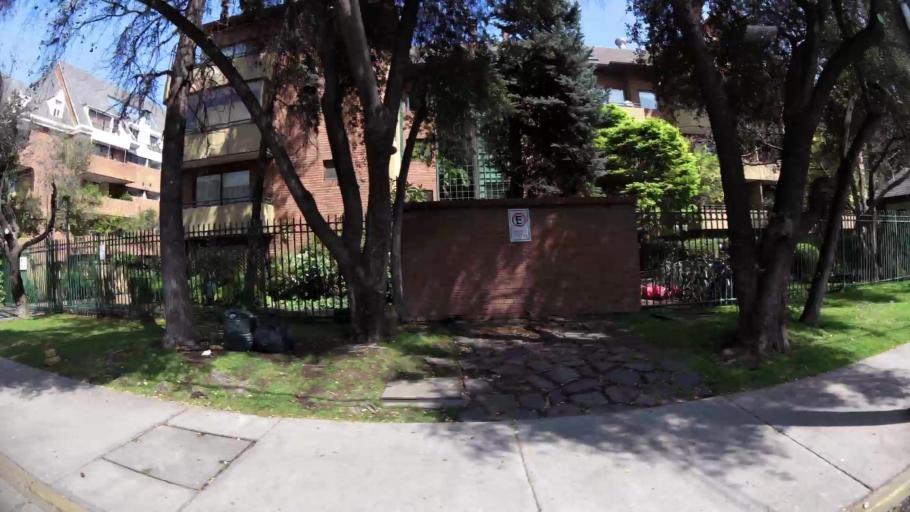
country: CL
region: Santiago Metropolitan
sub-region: Provincia de Santiago
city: Villa Presidente Frei, Nunoa, Santiago, Chile
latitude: -33.3962
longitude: -70.5774
